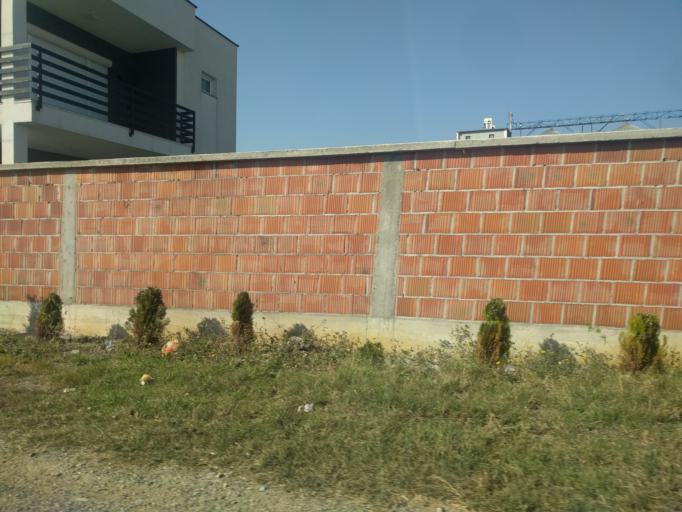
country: XK
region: Pristina
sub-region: Komuna e Gracanices
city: Glanica
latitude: 42.5970
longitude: 21.0199
